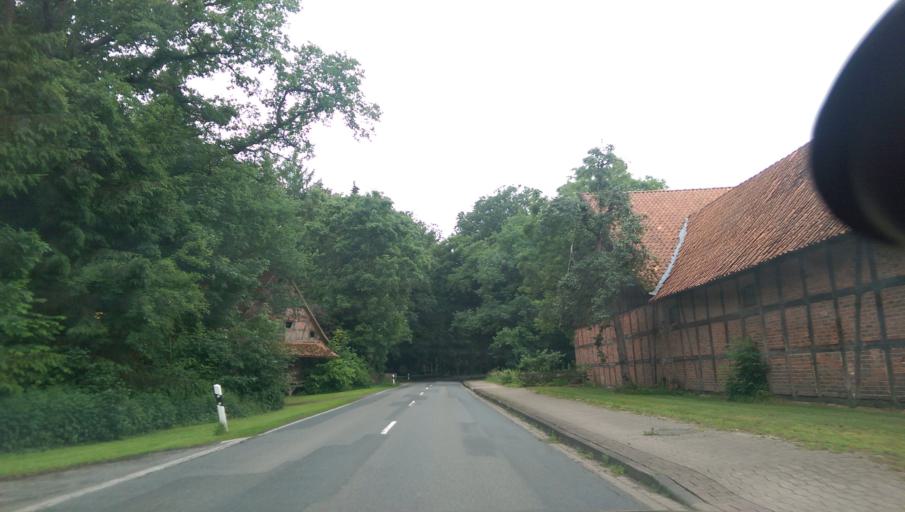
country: DE
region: Lower Saxony
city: Wittorf
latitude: 53.0004
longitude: 9.5368
